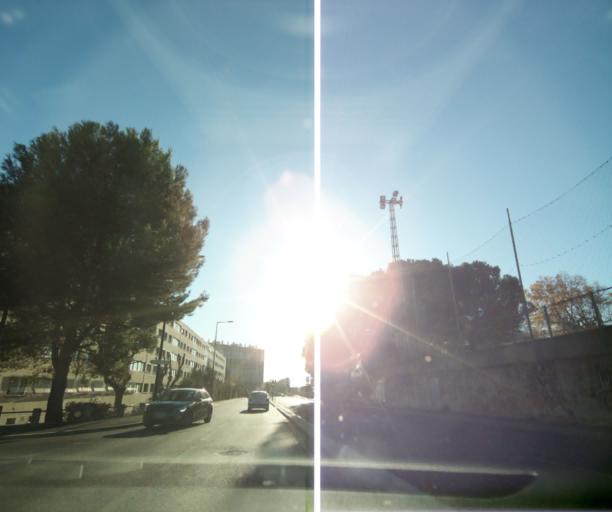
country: FR
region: Provence-Alpes-Cote d'Azur
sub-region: Departement des Bouches-du-Rhone
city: Plan-de-Cuques
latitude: 43.3365
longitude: 5.4347
